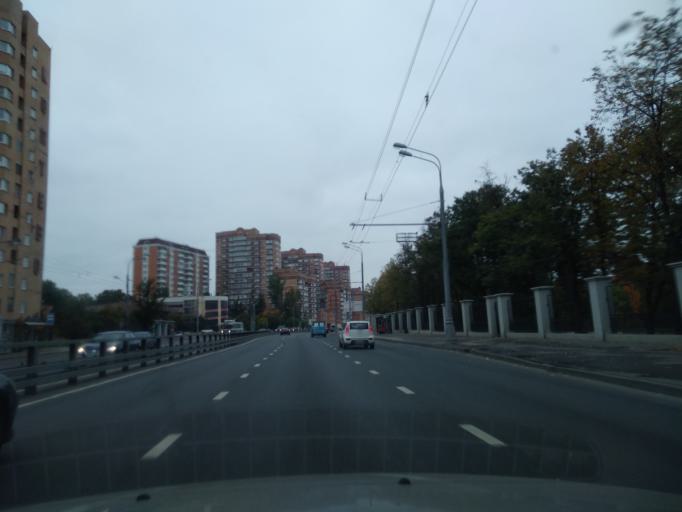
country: RU
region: Moskovskaya
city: Koptevo
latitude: 55.8325
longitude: 37.5327
